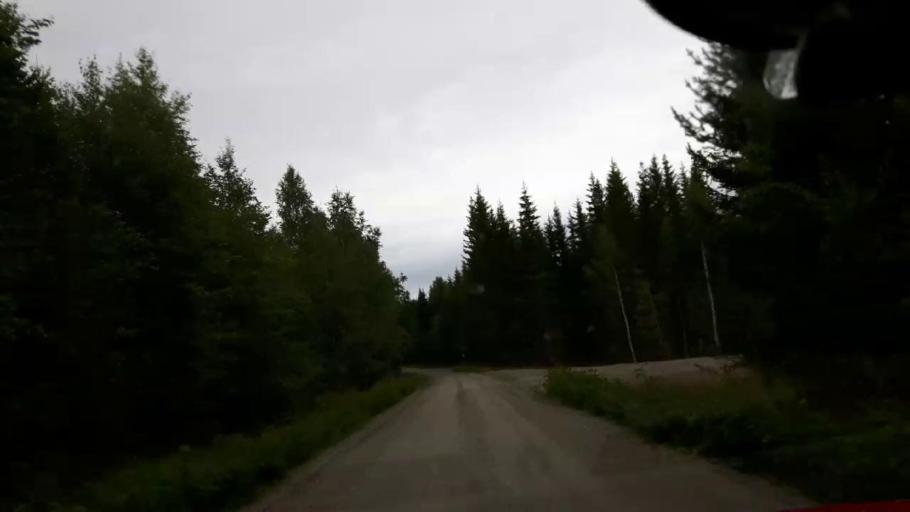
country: SE
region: Vaesternorrland
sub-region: Ange Kommun
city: Ange
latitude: 62.7985
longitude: 15.7704
